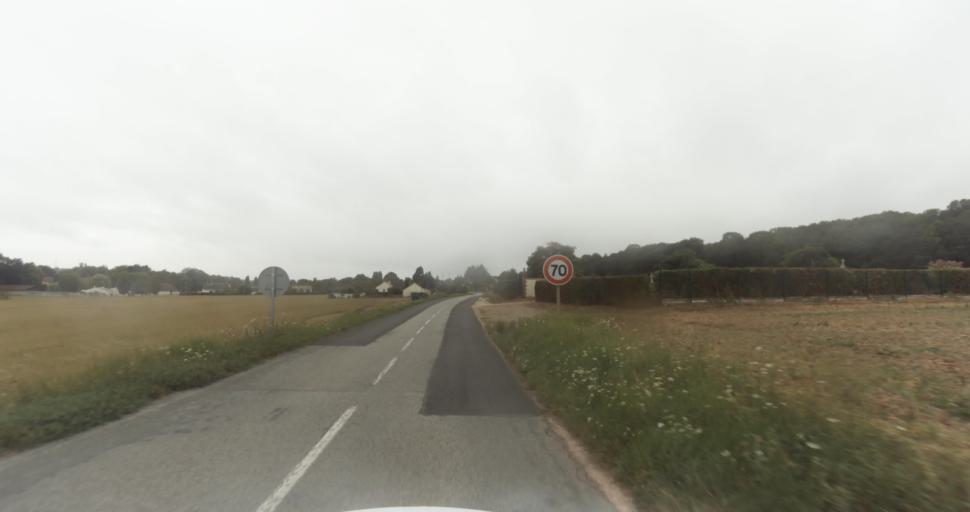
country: FR
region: Haute-Normandie
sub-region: Departement de l'Eure
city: Saint-Germain-sur-Avre
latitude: 48.7647
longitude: 1.2736
